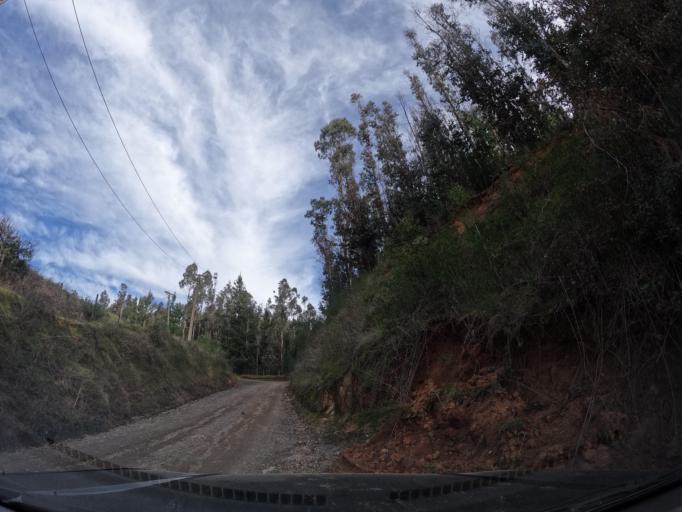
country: CL
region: Biobio
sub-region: Provincia de Concepcion
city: Chiguayante
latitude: -37.0159
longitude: -72.9101
